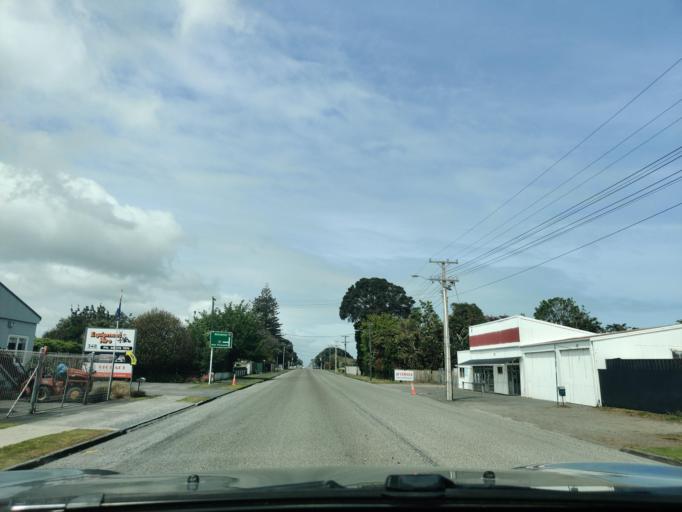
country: NZ
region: Taranaki
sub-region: South Taranaki District
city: Hawera
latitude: -39.5905
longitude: 174.2660
